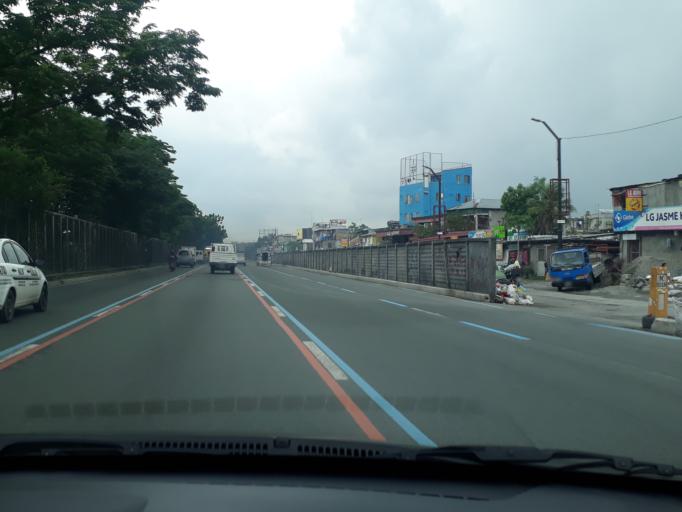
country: PH
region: Calabarzon
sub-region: Province of Rizal
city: Pateros
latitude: 14.5270
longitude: 121.0561
